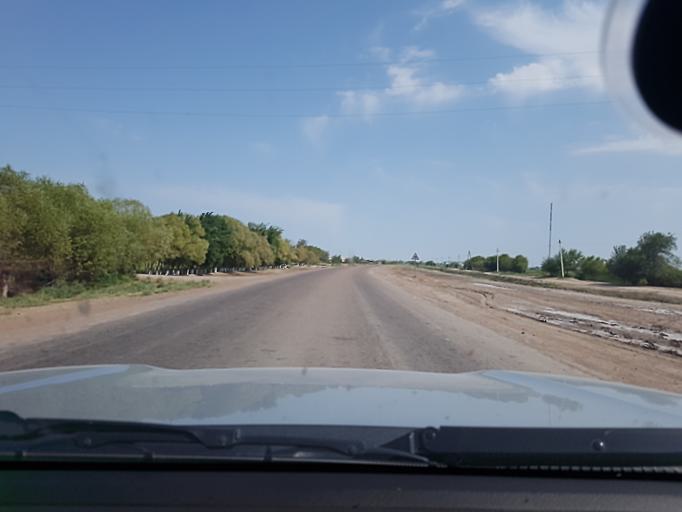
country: TM
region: Dasoguz
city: Boldumsaz
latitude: 42.1461
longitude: 59.6393
